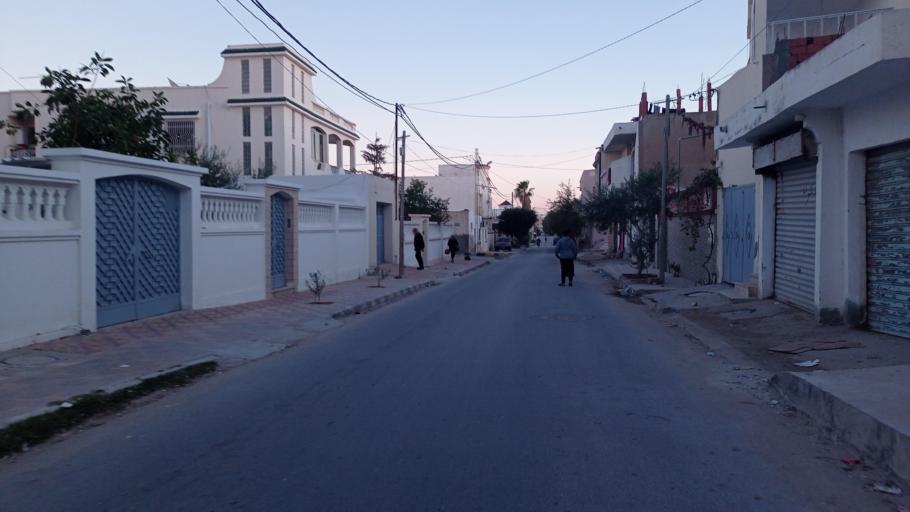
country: TN
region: Qabis
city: Gabes
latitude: 33.8473
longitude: 10.1139
